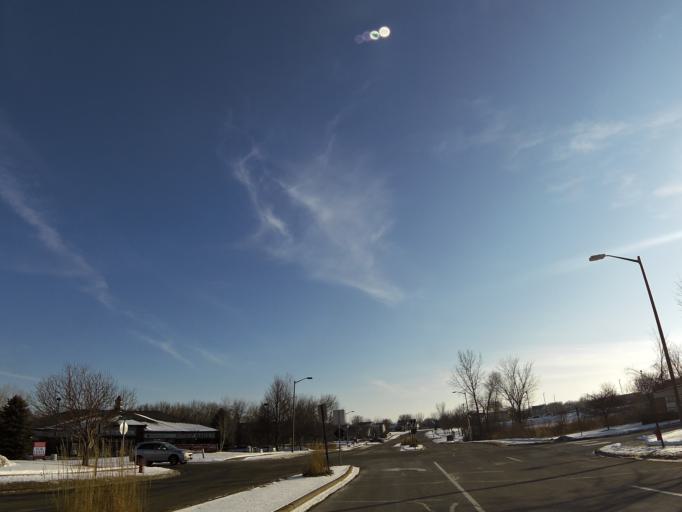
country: US
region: Minnesota
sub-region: Scott County
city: Savage
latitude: 44.7461
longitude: -93.3515
